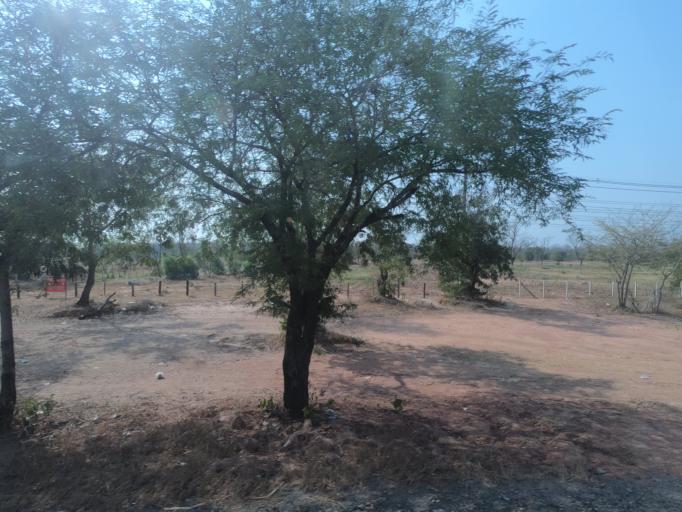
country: TH
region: Khon Kaen
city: Phon
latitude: 15.7653
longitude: 102.6064
